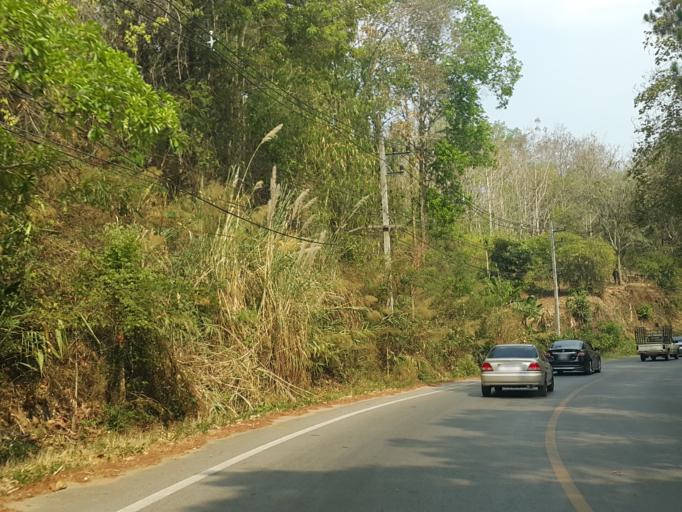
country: TH
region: Chiang Mai
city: Samoeng
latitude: 18.8991
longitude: 98.8488
